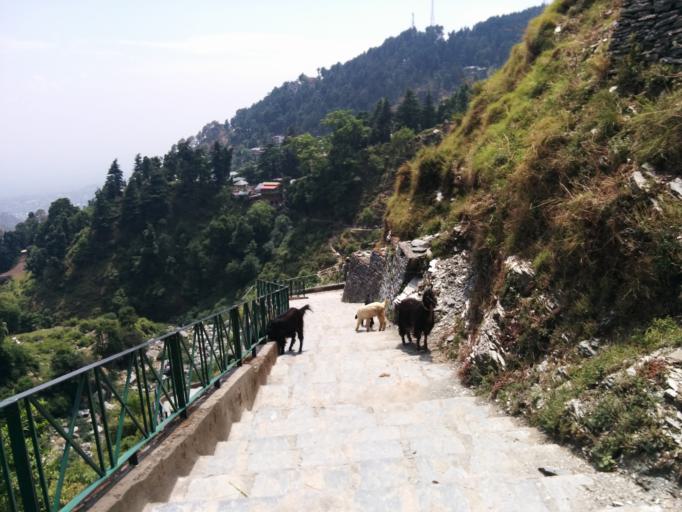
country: IN
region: Himachal Pradesh
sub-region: Kangra
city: Dharmsala
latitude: 32.2462
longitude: 76.3365
